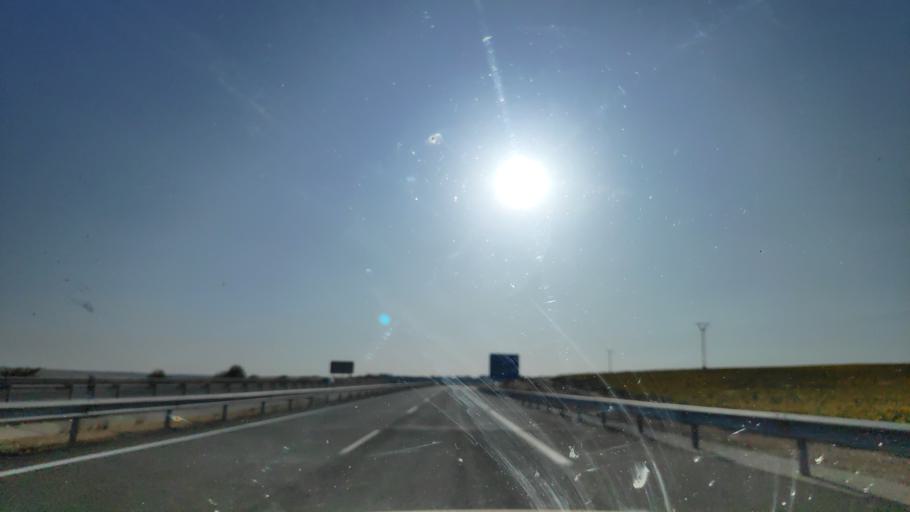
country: ES
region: Castille-La Mancha
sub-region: Provincia de Cuenca
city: Montalbo
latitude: 39.8791
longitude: -2.6395
